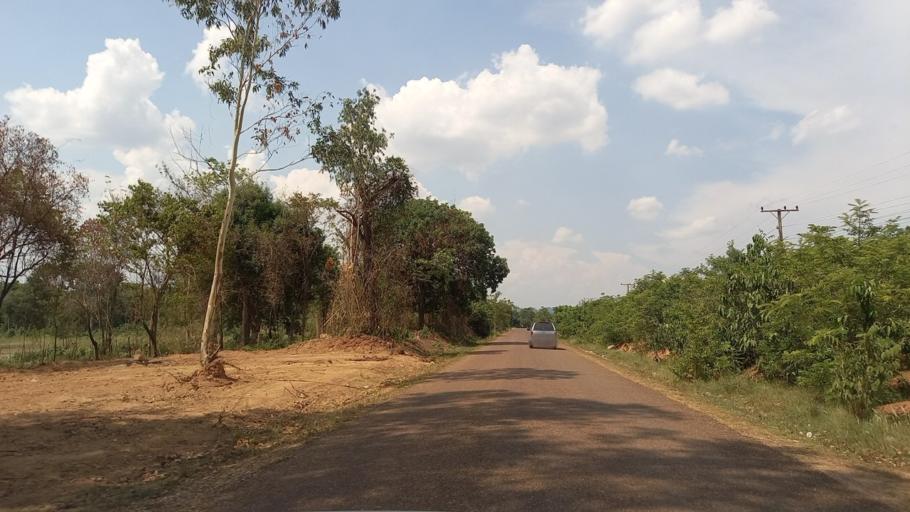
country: LA
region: Bolikhamxai
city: Muang Pakxan
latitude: 18.4234
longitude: 103.7066
